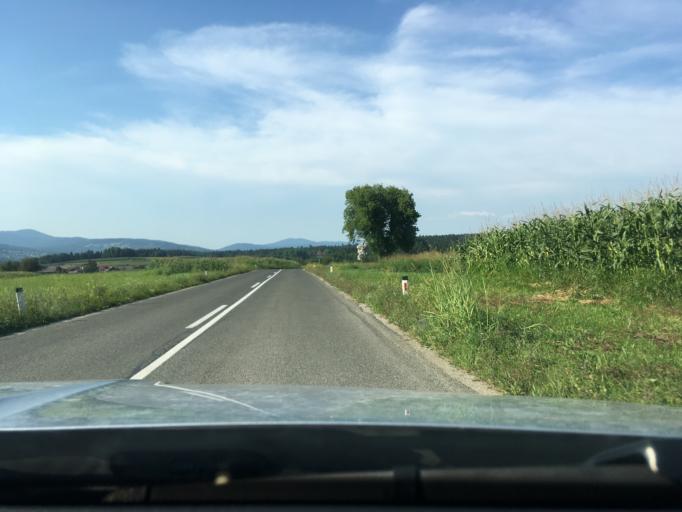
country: SI
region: Crnomelj
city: Crnomelj
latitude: 45.5339
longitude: 15.1633
